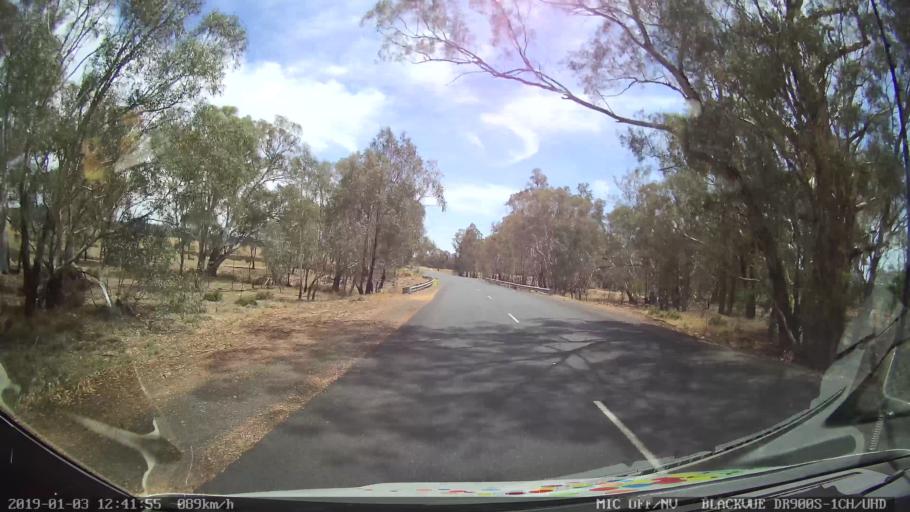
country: AU
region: New South Wales
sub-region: Weddin
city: Grenfell
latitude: -33.7932
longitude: 148.2149
